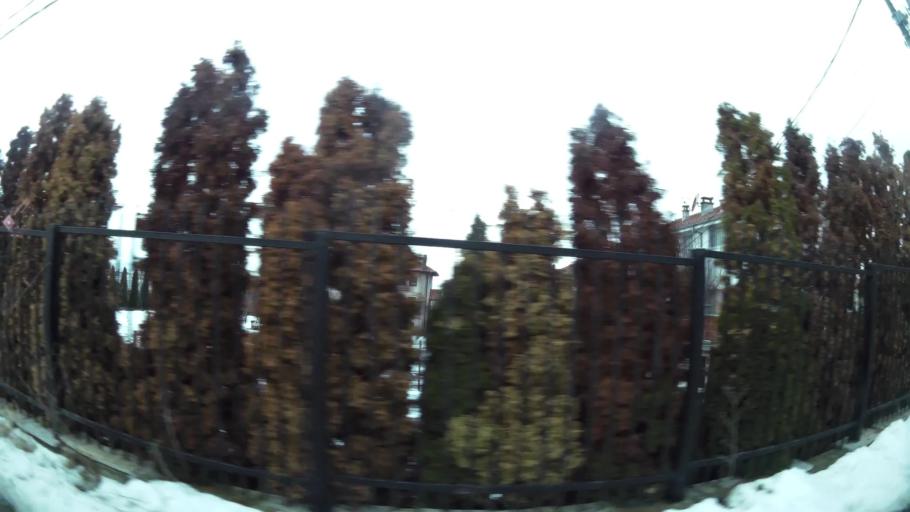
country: XK
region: Pristina
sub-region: Komuna e Prishtines
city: Pristina
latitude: 42.6249
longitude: 21.1630
